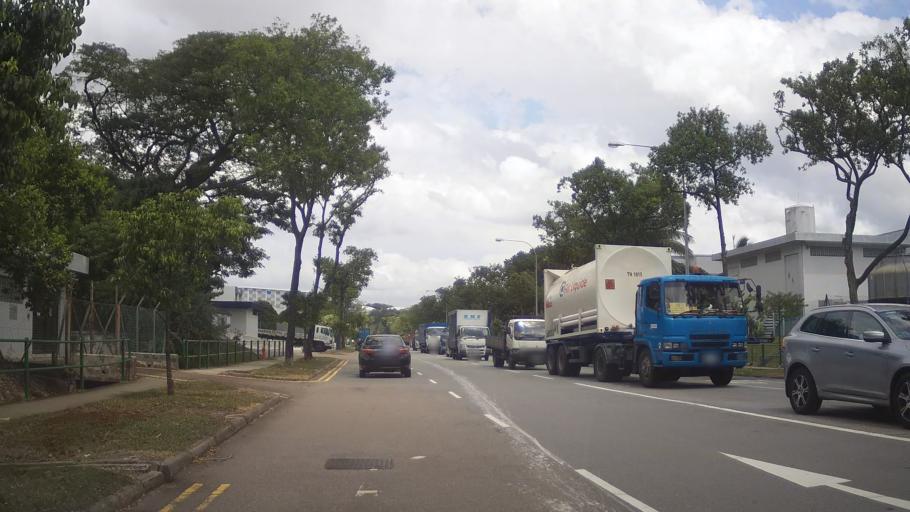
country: MY
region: Johor
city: Johor Bahru
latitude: 1.3241
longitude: 103.6704
